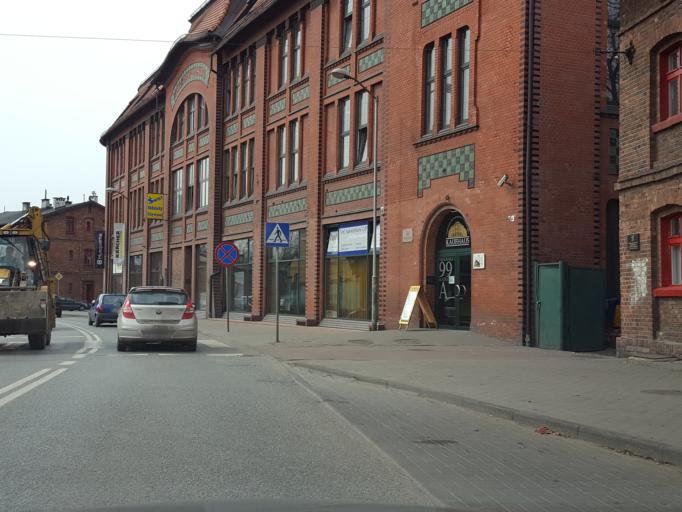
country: PL
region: Silesian Voivodeship
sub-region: Ruda Slaska
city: Ruda Slaska
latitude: 50.2942
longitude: 18.8749
